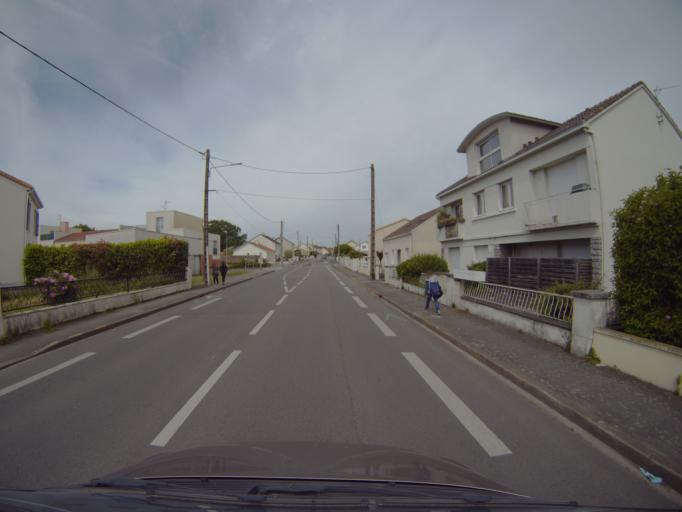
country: FR
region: Pays de la Loire
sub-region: Departement de la Loire-Atlantique
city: Reze
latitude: 47.1686
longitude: -1.5449
